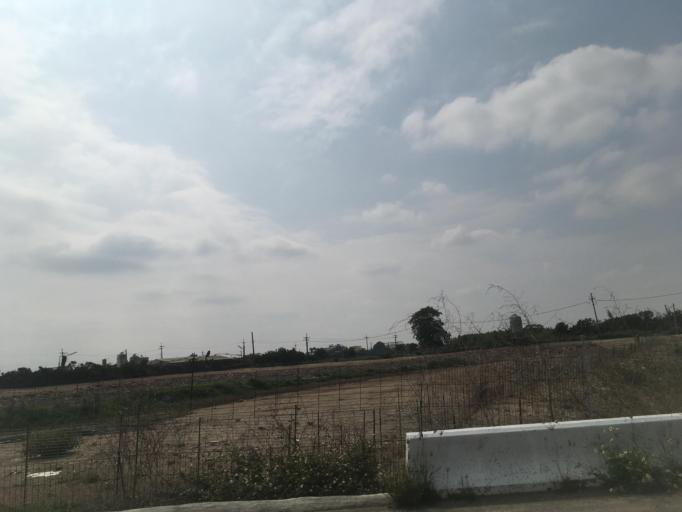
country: TW
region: Taiwan
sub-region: Yunlin
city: Douliu
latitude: 23.6954
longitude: 120.4541
